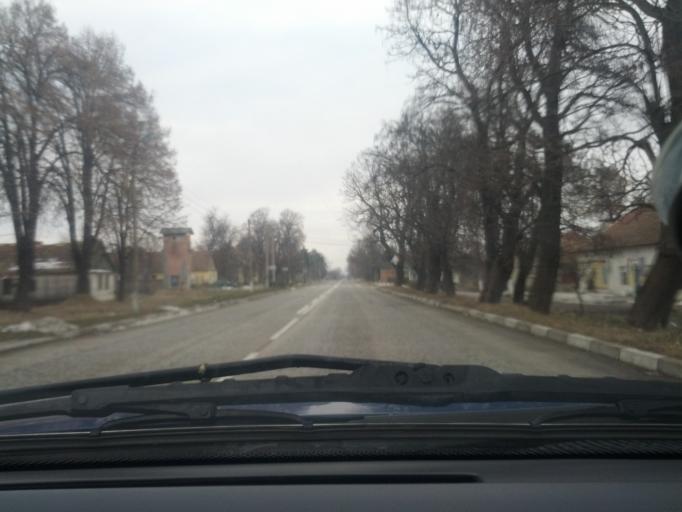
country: BG
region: Vratsa
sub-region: Obshtina Miziya
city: Miziya
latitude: 43.6492
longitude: 23.8431
